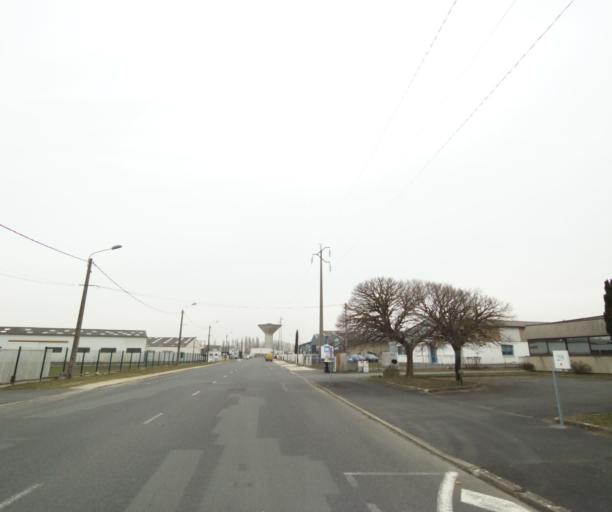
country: FR
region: Poitou-Charentes
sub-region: Departement des Deux-Sevres
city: Bessines
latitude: 46.3136
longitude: -0.4928
